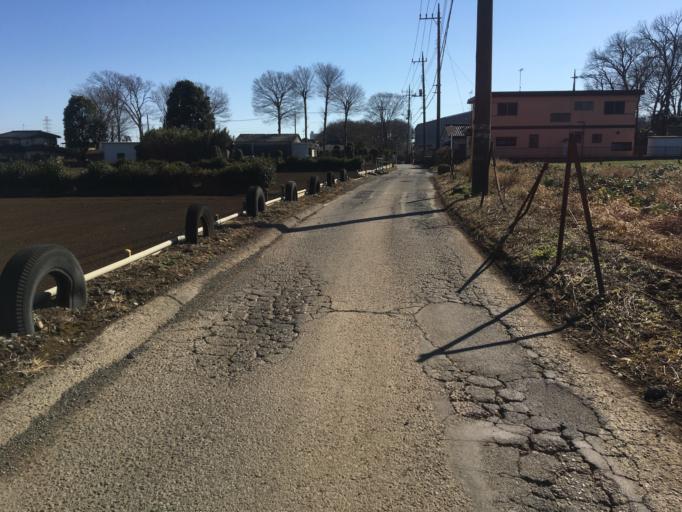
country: JP
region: Saitama
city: Oi
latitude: 35.8174
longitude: 139.5324
